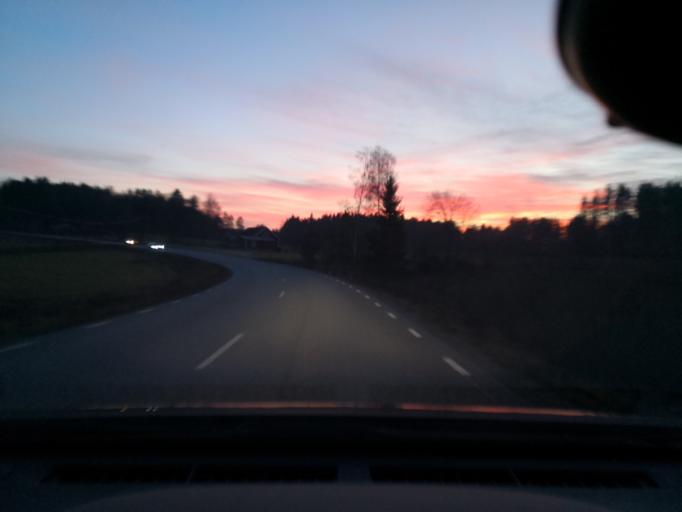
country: SE
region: OErebro
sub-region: Lindesbergs Kommun
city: Frovi
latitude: 59.3711
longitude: 15.4315
